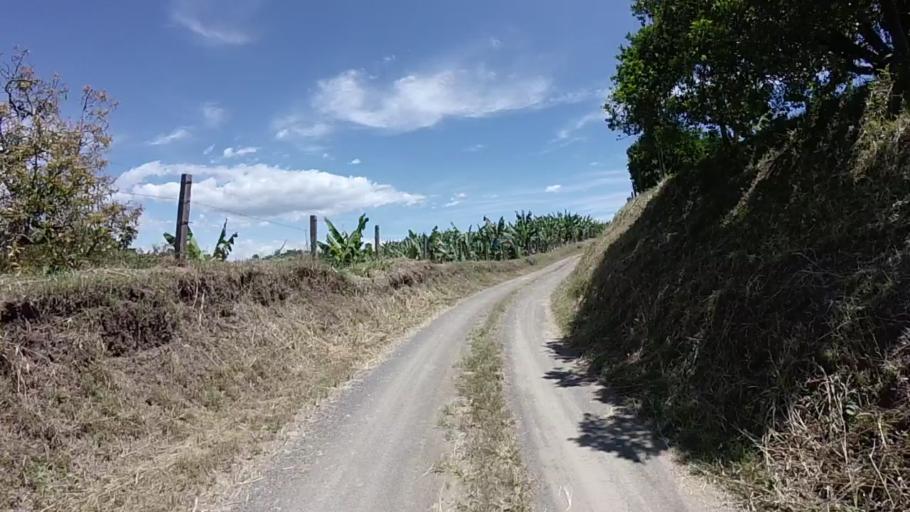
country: CO
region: Valle del Cauca
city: Alcala
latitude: 4.7063
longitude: -75.8235
